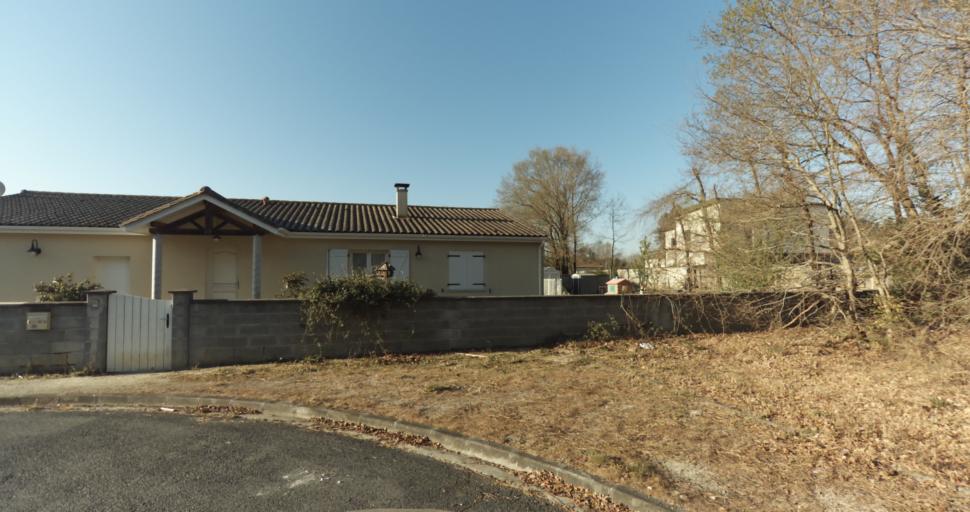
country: FR
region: Aquitaine
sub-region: Departement de la Gironde
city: Martignas-sur-Jalle
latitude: 44.8155
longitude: -0.7917
